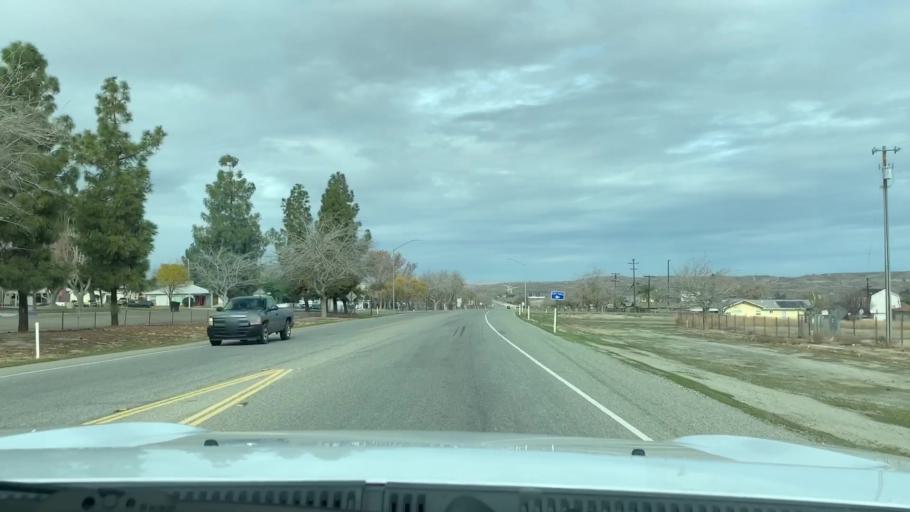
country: US
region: California
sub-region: Kern County
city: Taft
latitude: 35.1397
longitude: -119.4472
